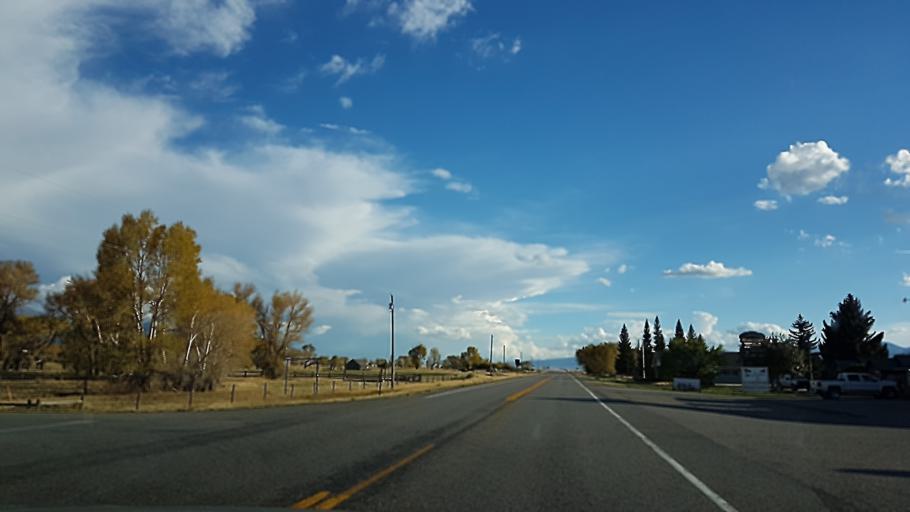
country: US
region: Montana
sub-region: Madison County
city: Virginia City
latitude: 45.2036
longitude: -111.6788
